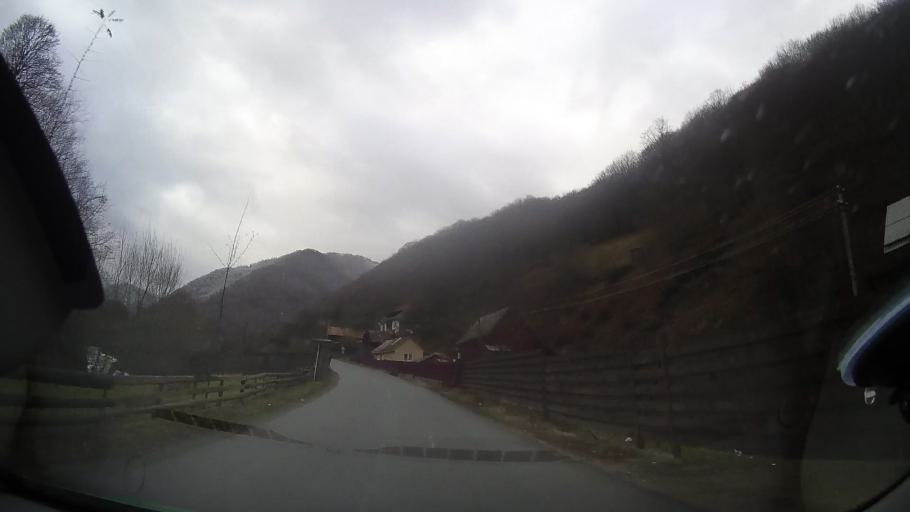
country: RO
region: Cluj
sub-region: Comuna Maguri-Racatau
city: Maguri-Racatau
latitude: 46.6542
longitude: 23.2050
